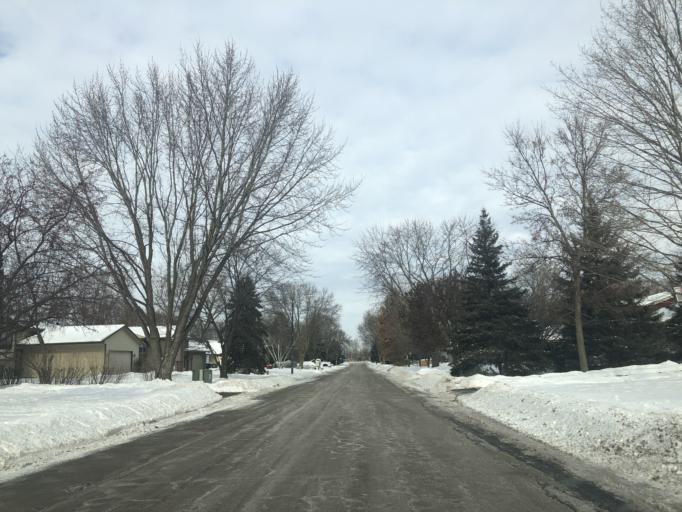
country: US
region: Minnesota
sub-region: Anoka County
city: Circle Pines
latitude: 45.1542
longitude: -93.1613
